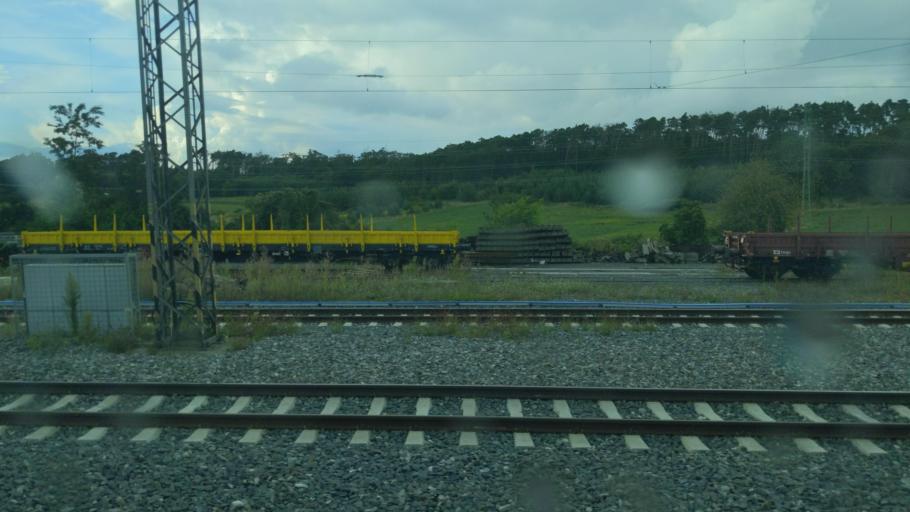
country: CZ
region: Central Bohemia
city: Poricany
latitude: 50.1118
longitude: 14.9257
